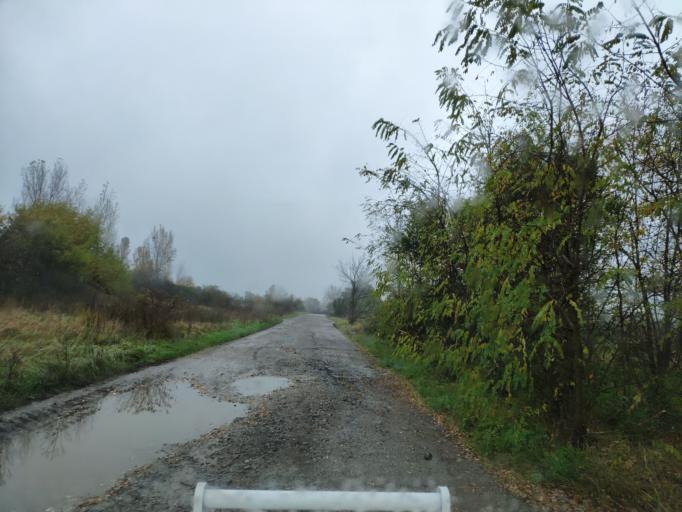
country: SK
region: Kosicky
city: Cierna nad Tisou
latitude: 48.4203
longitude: 21.9944
